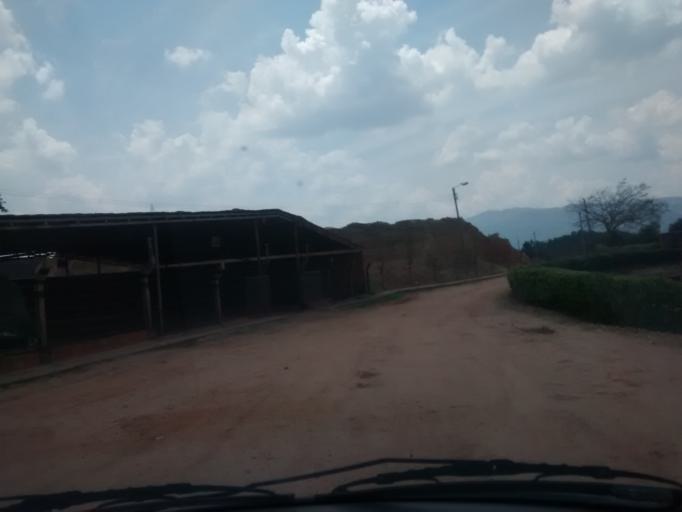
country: CO
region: Santander
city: Giron
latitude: 7.0710
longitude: -73.1280
